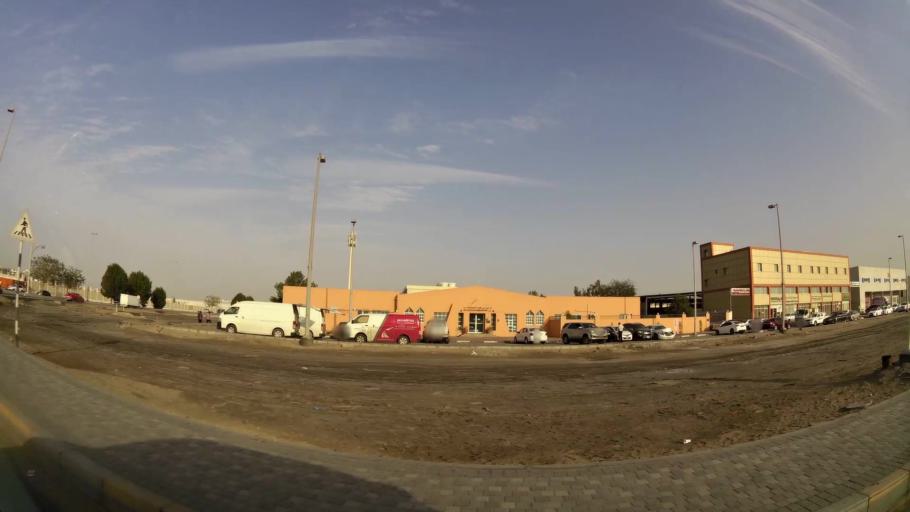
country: AE
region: Abu Dhabi
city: Abu Dhabi
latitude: 24.3548
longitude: 54.5174
